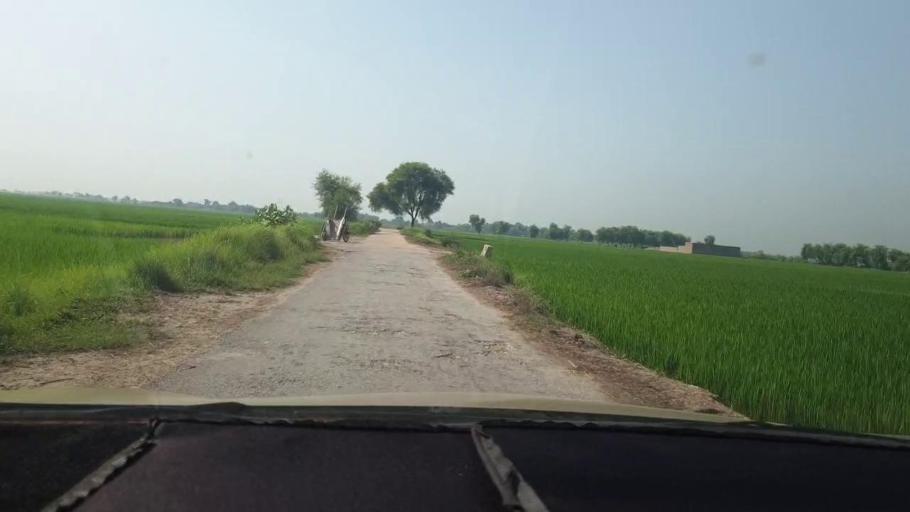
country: PK
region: Sindh
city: Kambar
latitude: 27.5770
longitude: 68.0556
